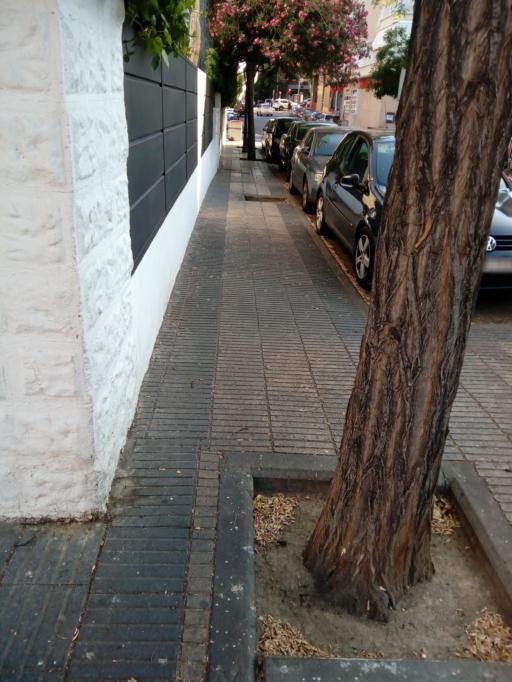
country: ES
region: Madrid
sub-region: Provincia de Madrid
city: Retiro
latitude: 40.4077
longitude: -3.6732
